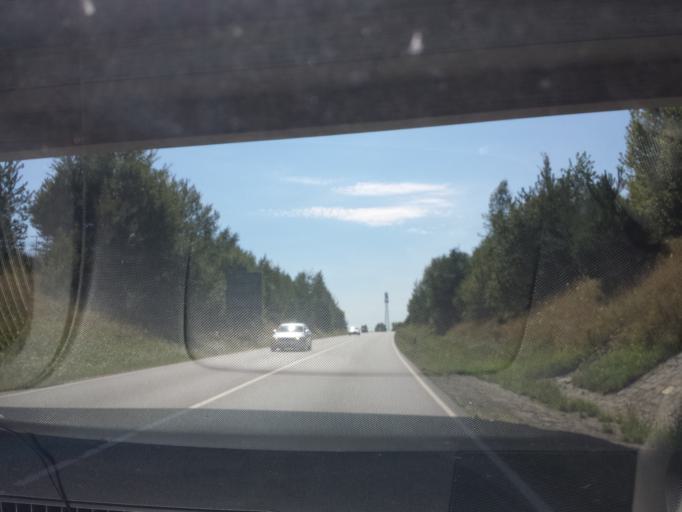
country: DE
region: Bavaria
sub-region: Upper Palatinate
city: Traitsching
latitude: 49.1660
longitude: 12.6564
